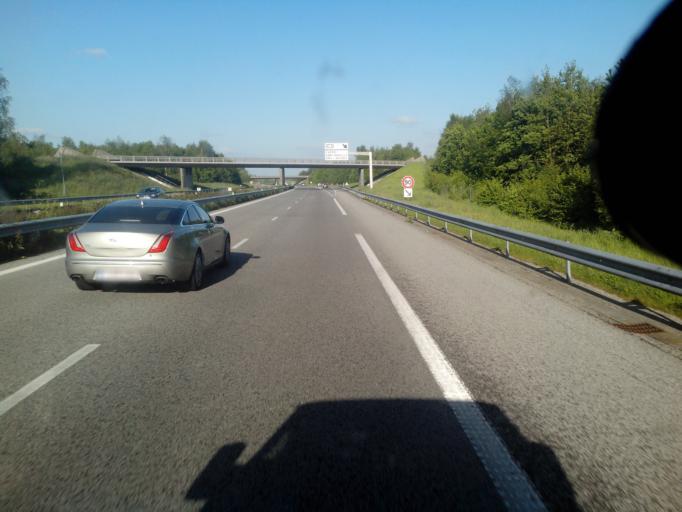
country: FR
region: Haute-Normandie
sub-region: Departement de la Seine-Maritime
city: Fauville-en-Caux
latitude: 49.6298
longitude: 0.6379
